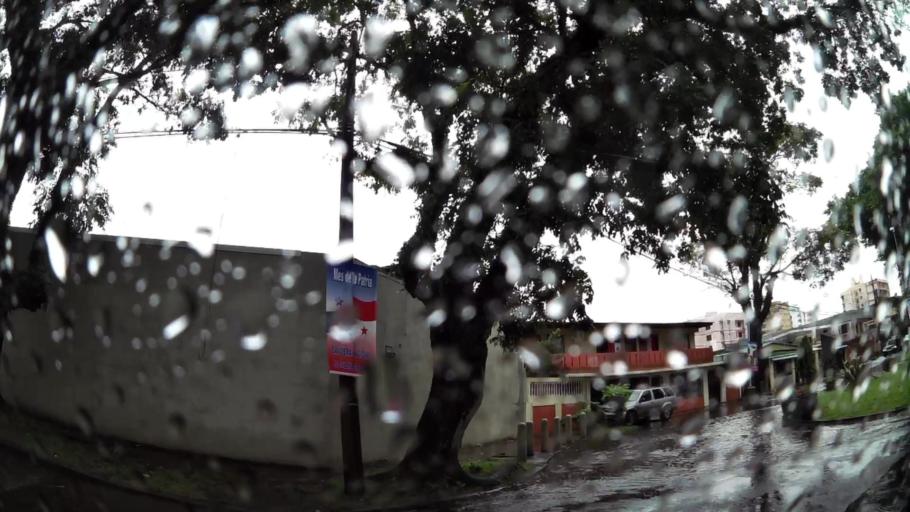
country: PA
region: Colon
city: Colon
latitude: 9.3616
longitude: -79.8965
